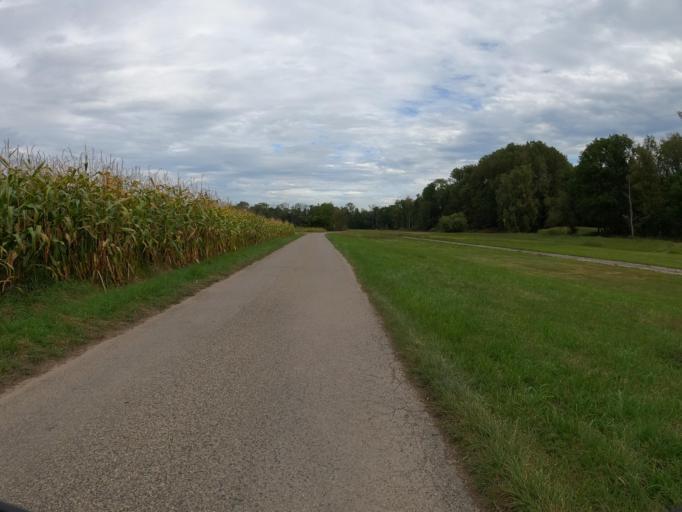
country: DE
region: Bavaria
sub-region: Swabia
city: Holzheim
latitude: 48.3897
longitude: 10.0761
